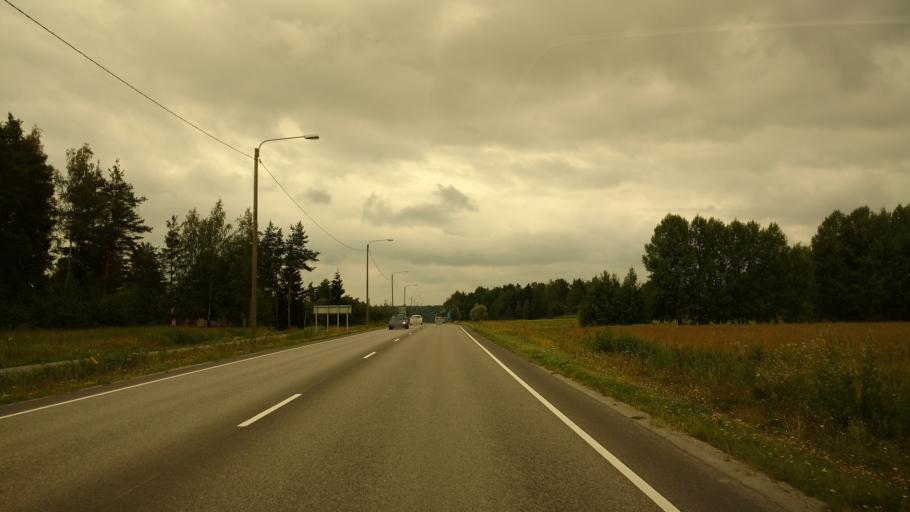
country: FI
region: Varsinais-Suomi
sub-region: Salo
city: Halikko
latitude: 60.4182
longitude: 23.0505
